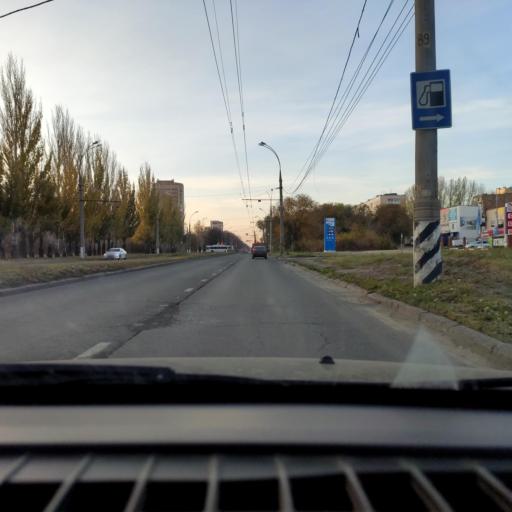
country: RU
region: Samara
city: Tol'yatti
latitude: 53.5400
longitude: 49.2788
